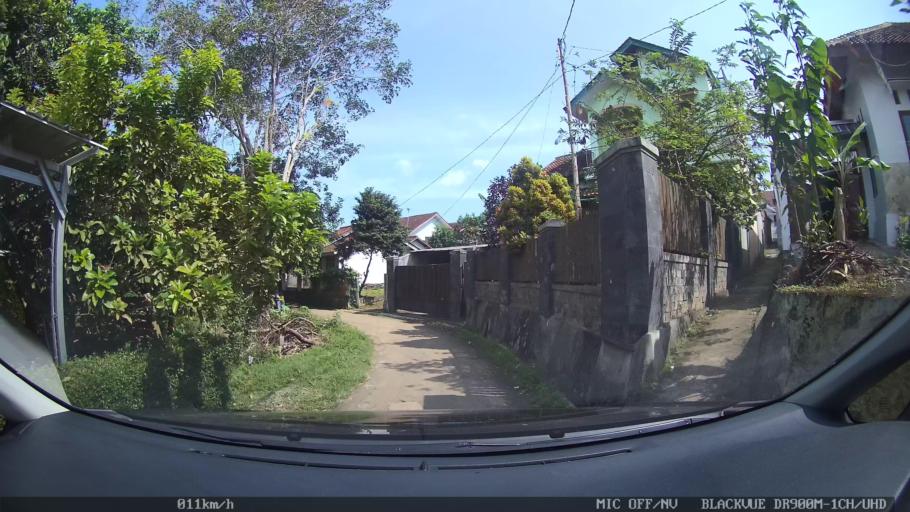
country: ID
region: Lampung
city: Kedaton
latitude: -5.4006
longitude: 105.2380
